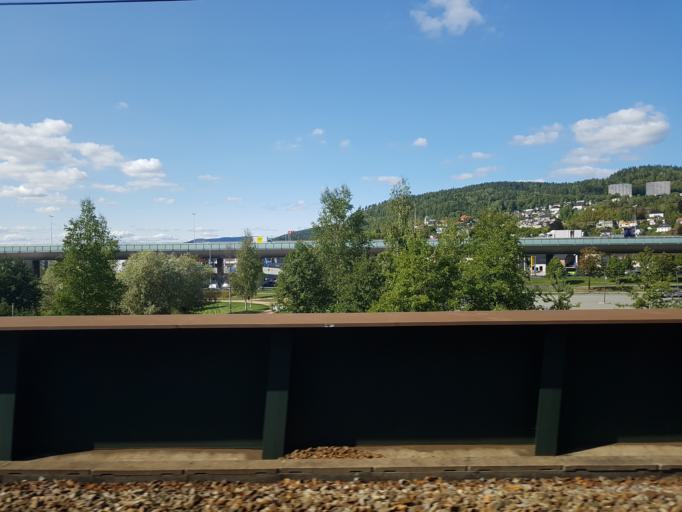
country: NO
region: Buskerud
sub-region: Drammen
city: Drammen
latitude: 59.7400
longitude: 10.2287
